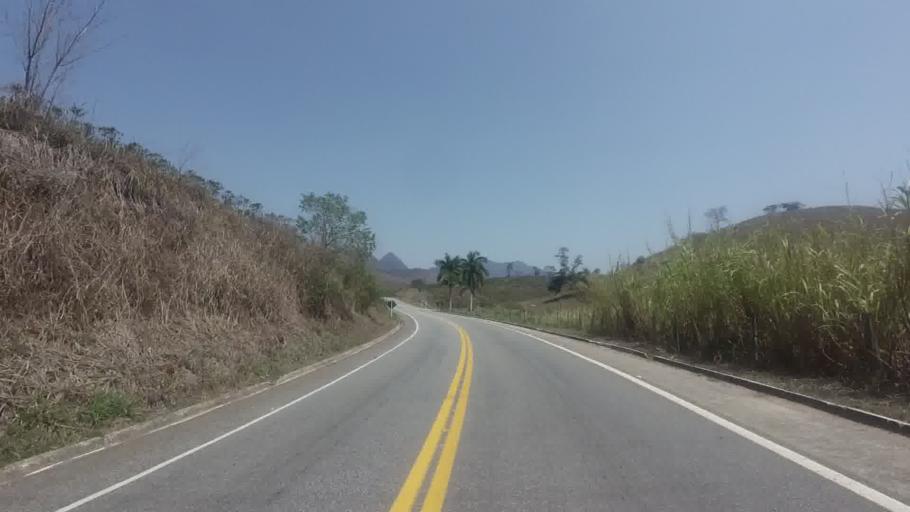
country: BR
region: Espirito Santo
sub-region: Jeronimo Monteiro
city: Jeronimo Monteiro
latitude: -20.9120
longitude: -41.3025
